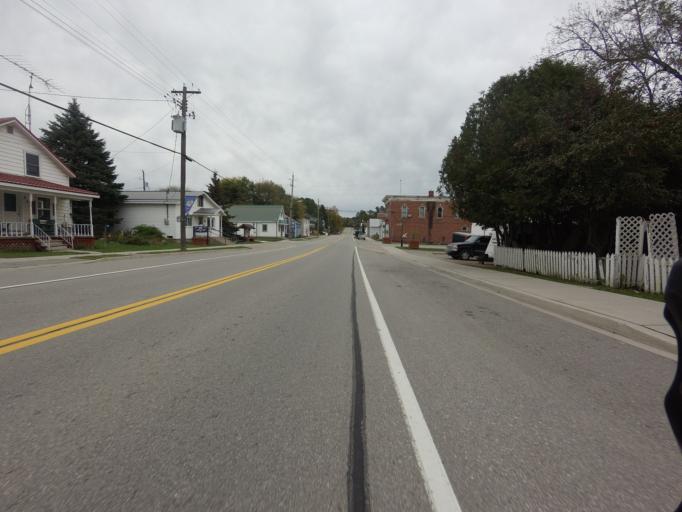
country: CA
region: Ontario
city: Gananoque
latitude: 44.5503
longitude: -76.1245
